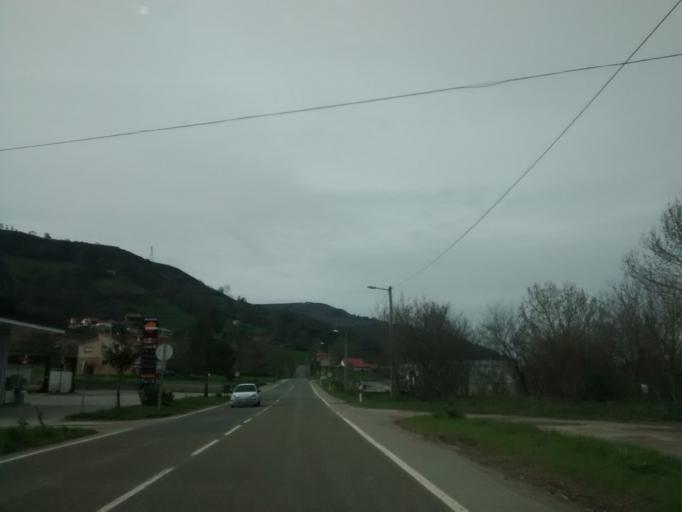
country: ES
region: Cantabria
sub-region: Provincia de Cantabria
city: Santiurde de Toranzo
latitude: 43.2192
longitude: -3.9436
